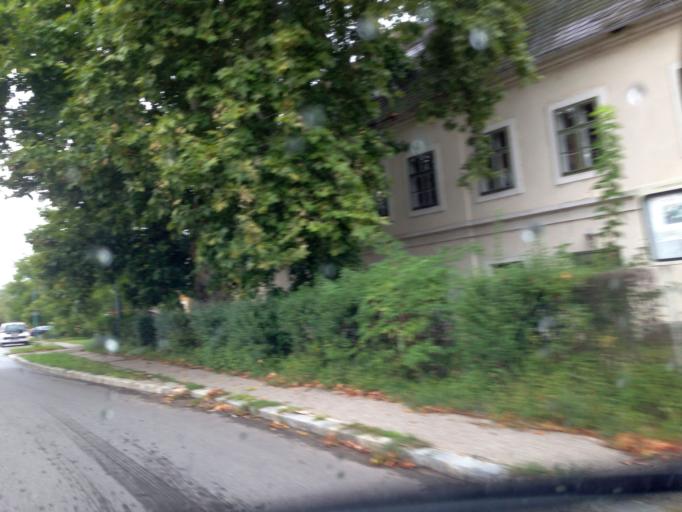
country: AT
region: Burgenland
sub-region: Politischer Bezirk Neusiedl am See
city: Potzneusiedl
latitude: 48.0449
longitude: 16.9481
